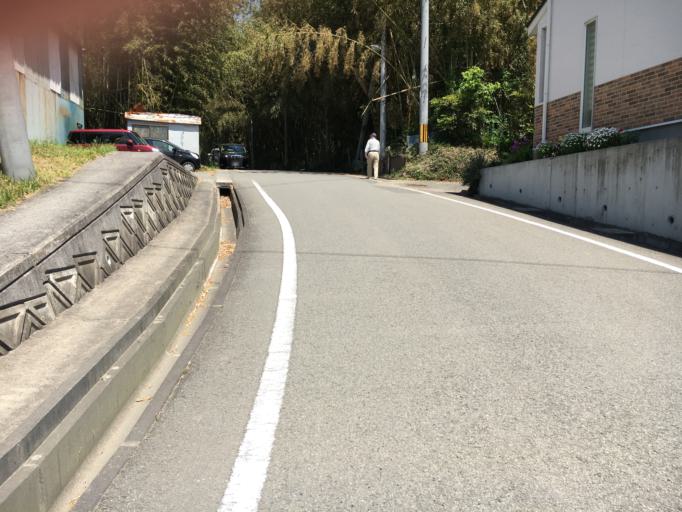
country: JP
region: Kyoto
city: Kameoka
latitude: 35.0254
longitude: 135.5930
